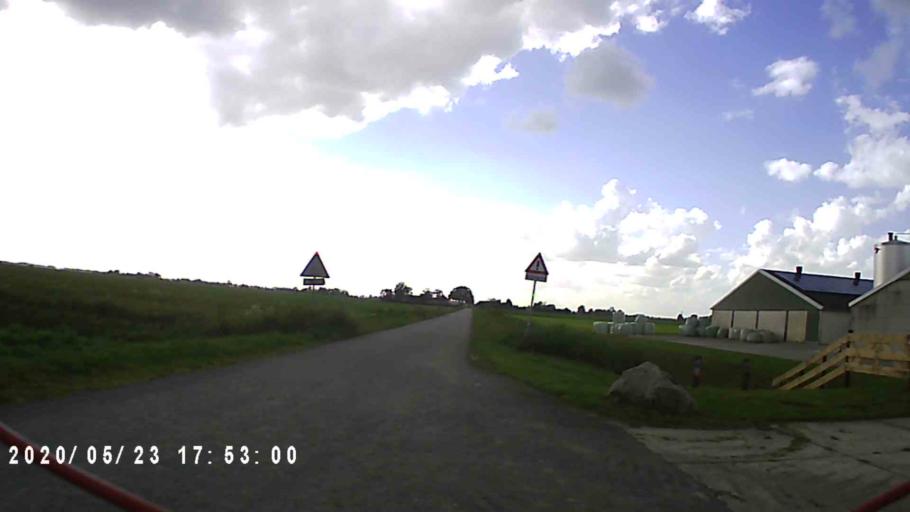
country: NL
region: Groningen
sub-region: Gemeente Slochteren
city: Slochteren
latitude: 53.2435
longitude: 6.7553
